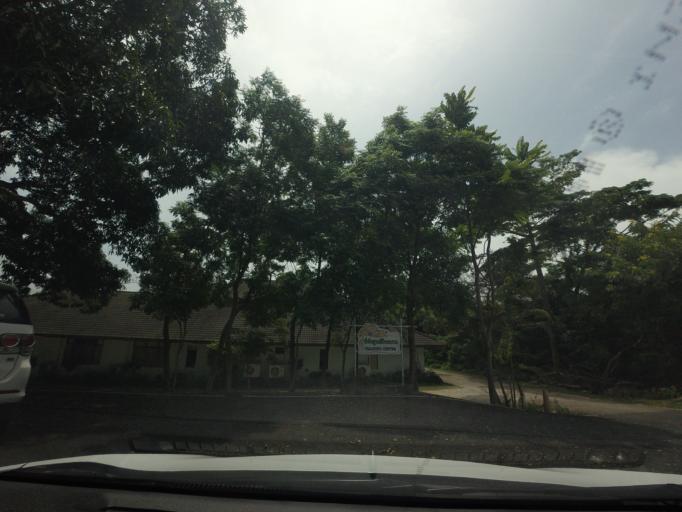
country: TH
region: Chon Buri
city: Ban Bueng
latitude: 13.2127
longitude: 101.0700
